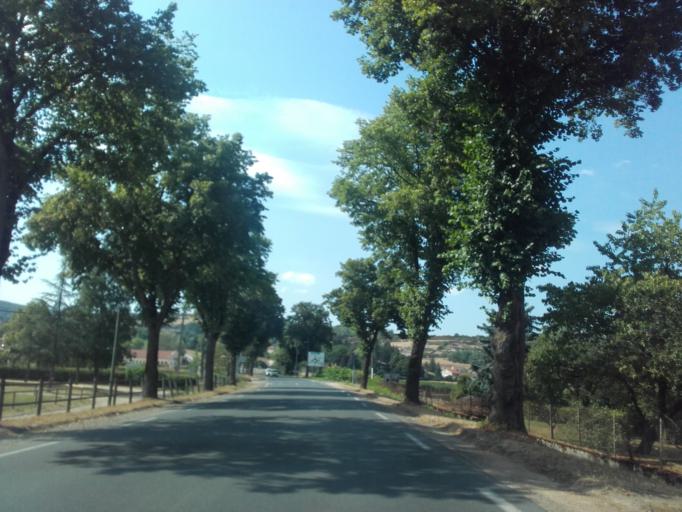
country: FR
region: Bourgogne
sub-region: Departement de Saone-et-Loire
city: Cluny
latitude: 46.4373
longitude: 4.6627
